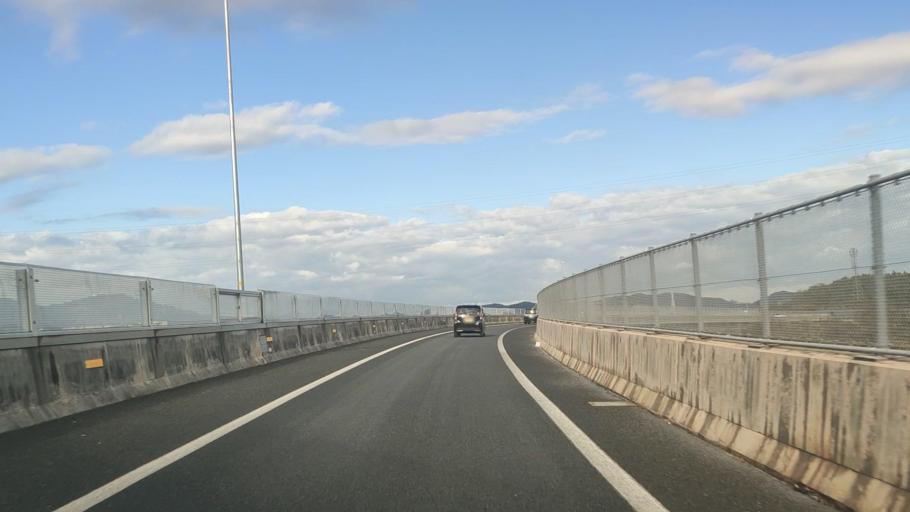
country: JP
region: Fukuoka
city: Kitakyushu
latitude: 33.8157
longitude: 130.8865
